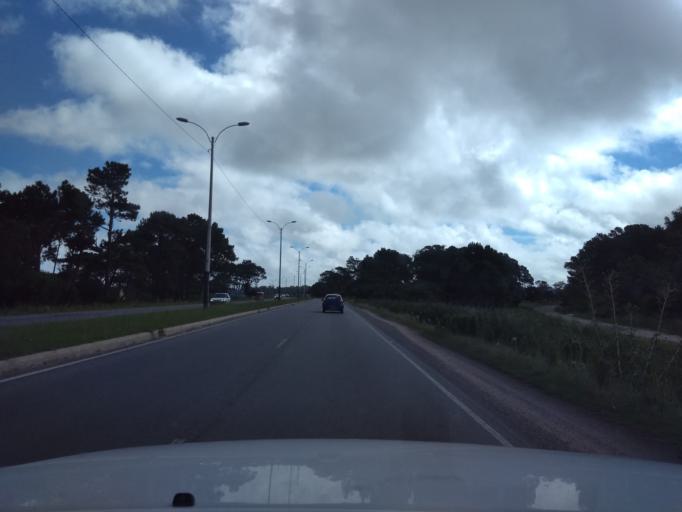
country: UY
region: Canelones
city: Barra de Carrasco
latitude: -34.8679
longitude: -56.0108
